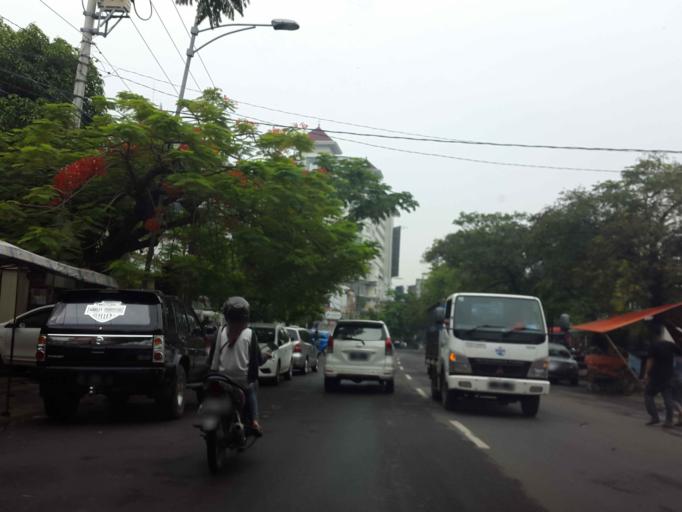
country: ID
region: Central Java
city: Semarang
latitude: -6.9887
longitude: 110.4263
